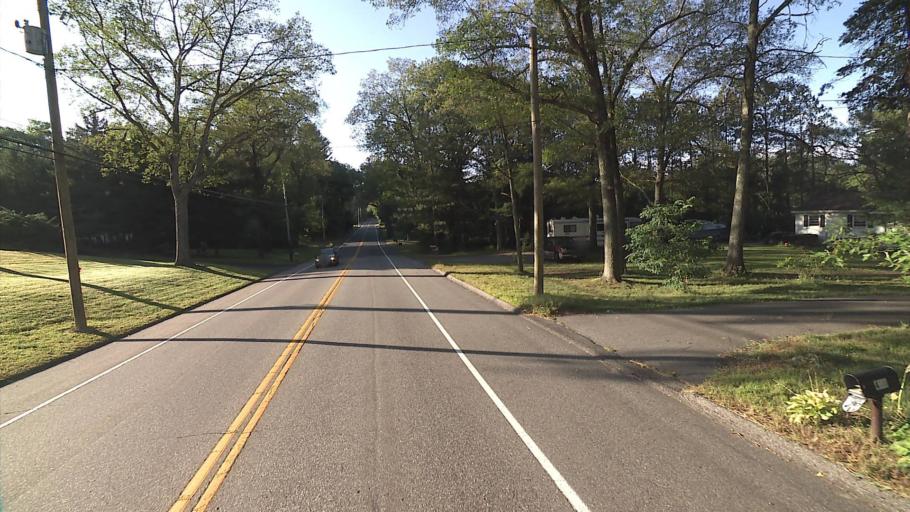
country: US
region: Connecticut
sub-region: Tolland County
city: Mansfield City
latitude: 41.7552
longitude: -72.2630
